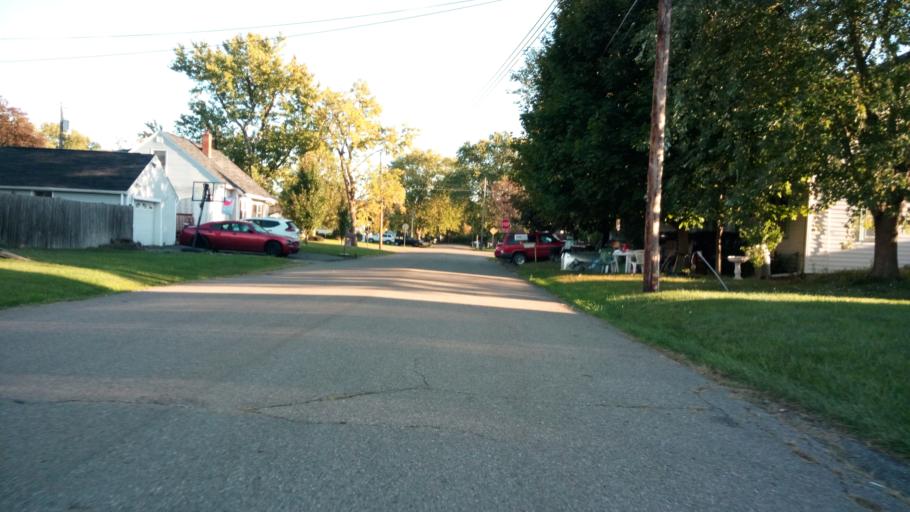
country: US
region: New York
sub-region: Chemung County
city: Elmira
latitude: 42.0744
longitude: -76.8195
